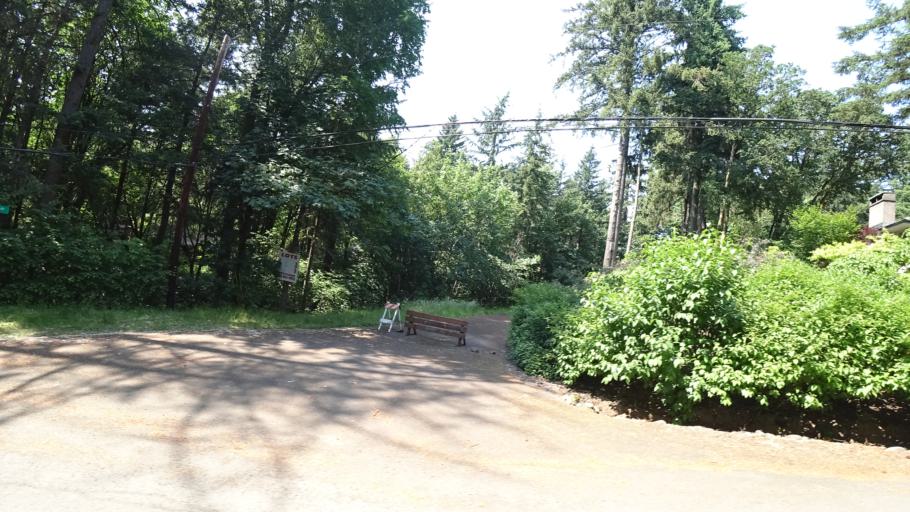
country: US
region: Oregon
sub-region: Clackamas County
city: Happy Valley
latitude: 45.4455
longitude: -122.5585
